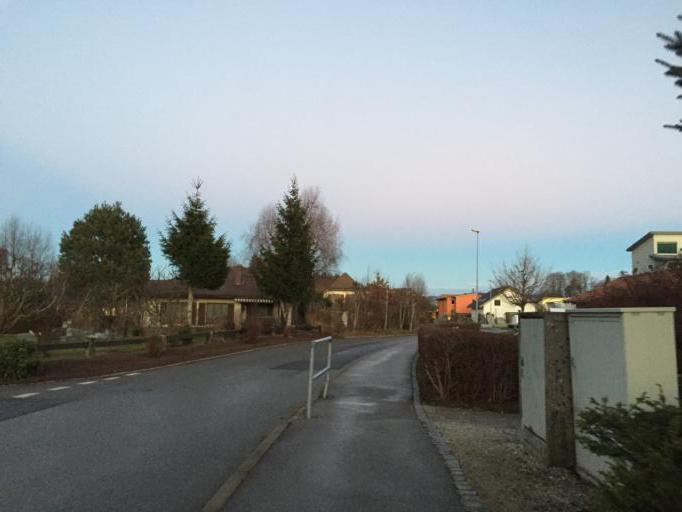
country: CH
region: Fribourg
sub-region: Sense District
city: Heitenried
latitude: 46.8270
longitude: 7.3061
